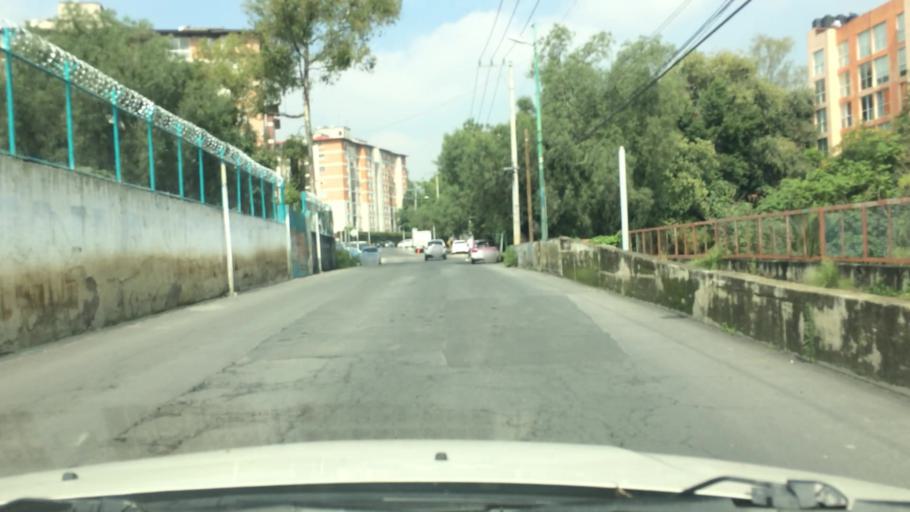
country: MX
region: Mexico City
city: Magdalena Contreras
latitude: 19.3473
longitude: -99.2150
